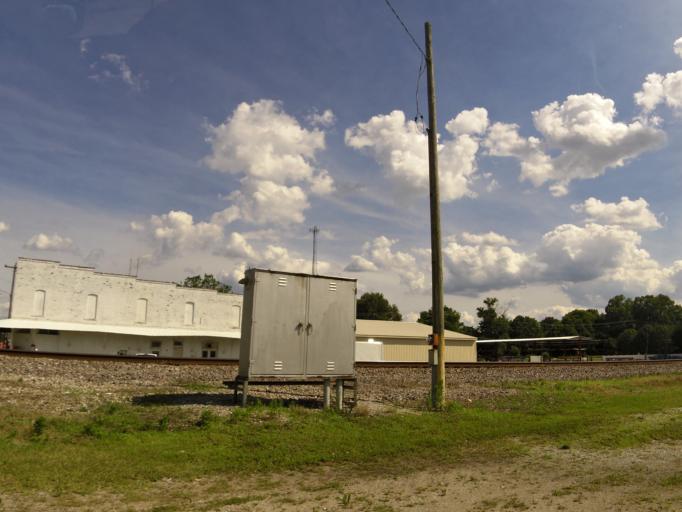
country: US
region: Tennessee
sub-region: Gibson County
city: Milan
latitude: 35.9734
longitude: -88.6807
